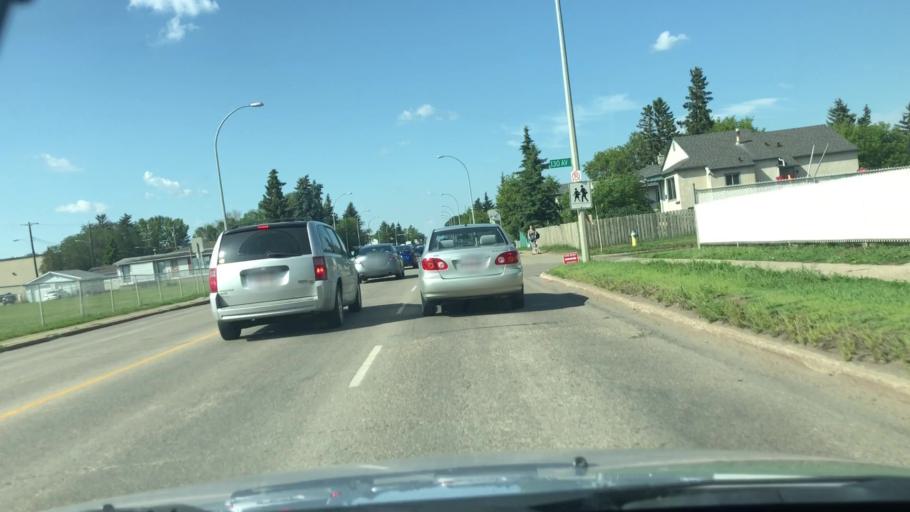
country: CA
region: Alberta
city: Edmonton
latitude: 53.5888
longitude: -113.4429
